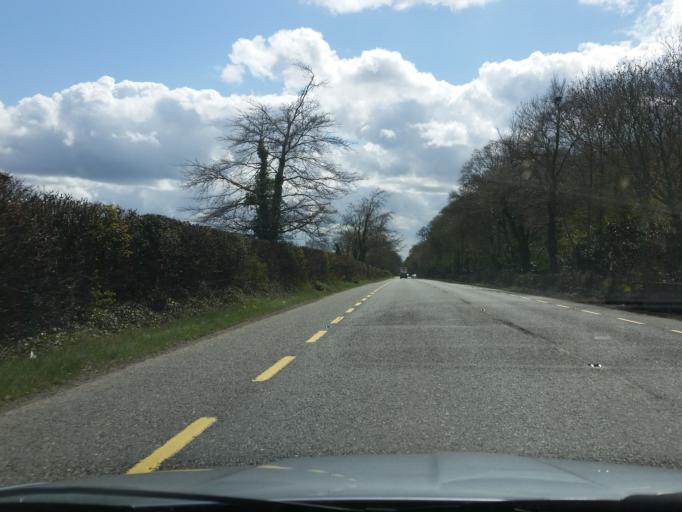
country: IE
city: Kentstown
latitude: 53.6347
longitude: -6.4944
